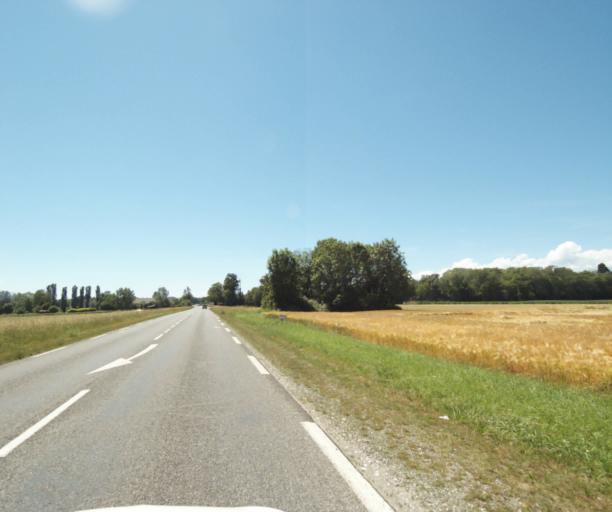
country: FR
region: Rhone-Alpes
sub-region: Departement de la Haute-Savoie
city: Veigy-Foncenex
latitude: 46.2798
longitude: 6.2515
